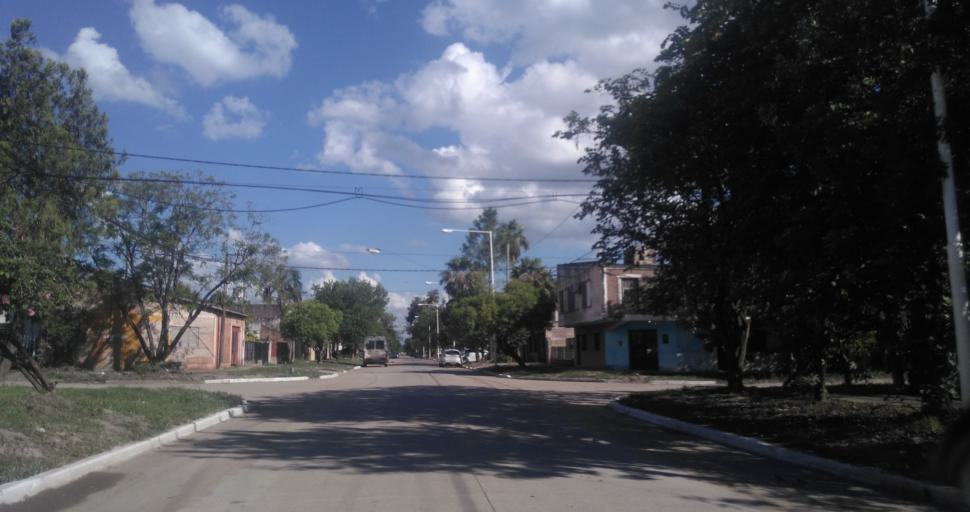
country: AR
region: Chaco
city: Resistencia
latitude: -27.4670
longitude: -58.9739
